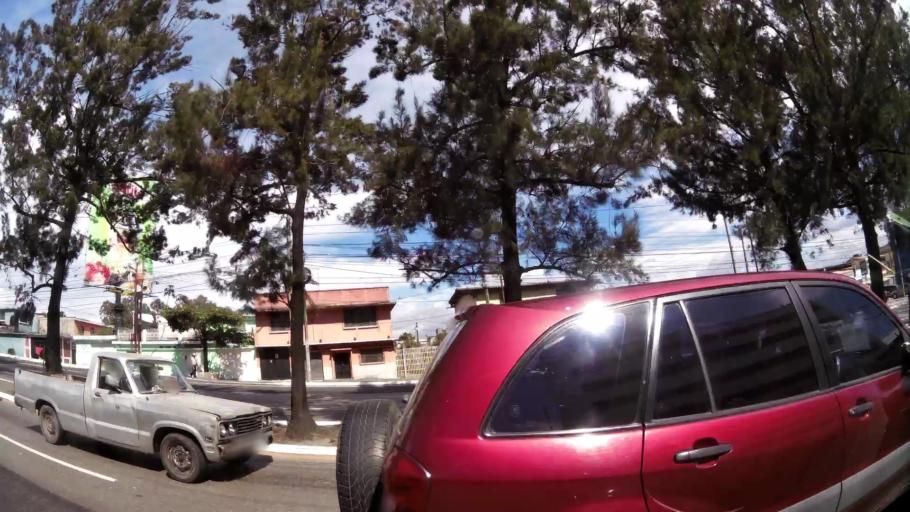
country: GT
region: Guatemala
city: Guatemala City
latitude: 14.6309
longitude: -90.5572
